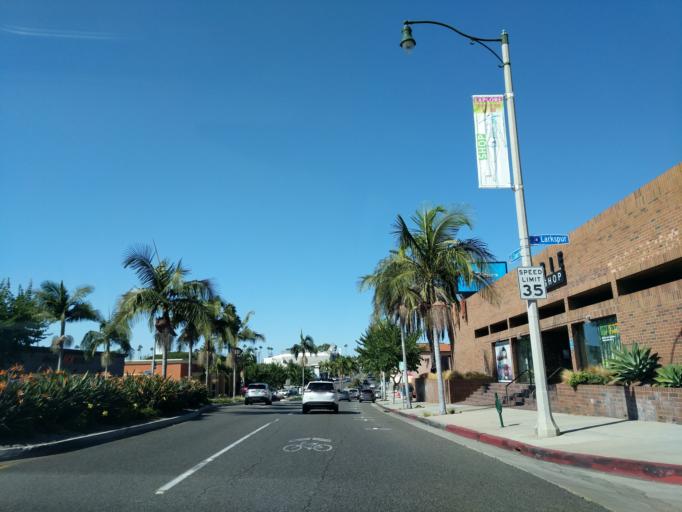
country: US
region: California
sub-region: Orange County
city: San Joaquin Hills
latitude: 33.5973
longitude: -117.8713
